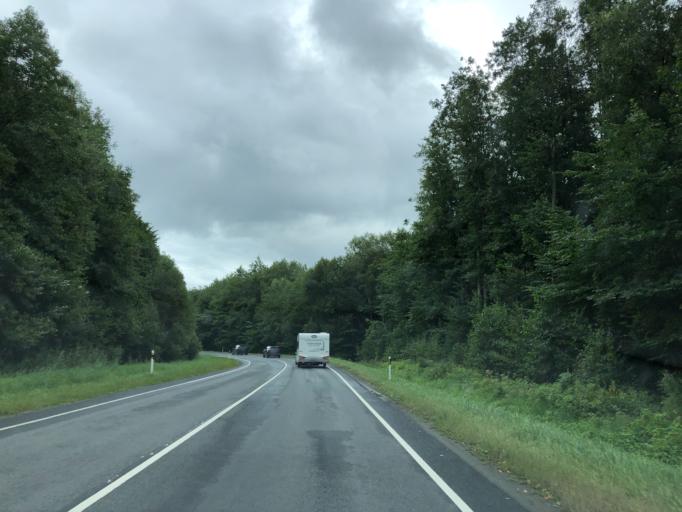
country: EE
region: Laeaene
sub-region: Haapsalu linn
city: Haapsalu
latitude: 58.9176
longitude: 23.4850
